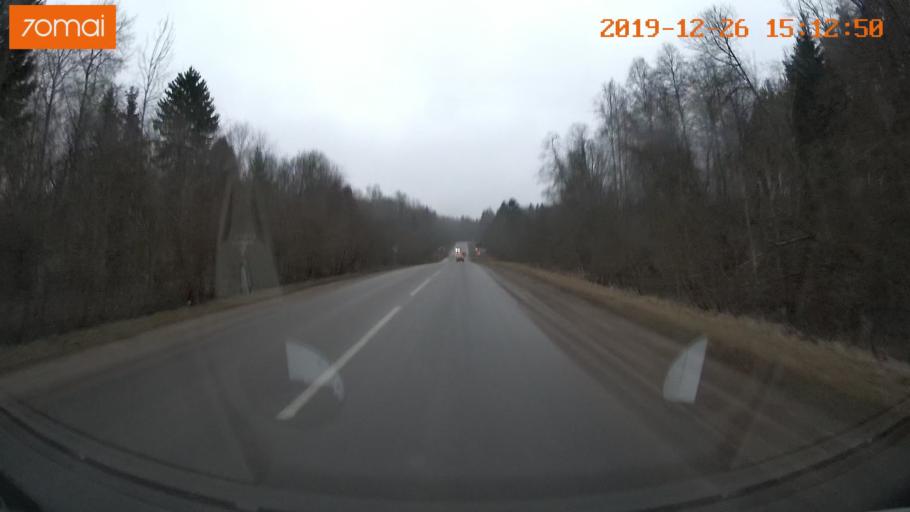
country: RU
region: Jaroslavl
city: Rybinsk
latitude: 58.1243
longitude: 38.8806
